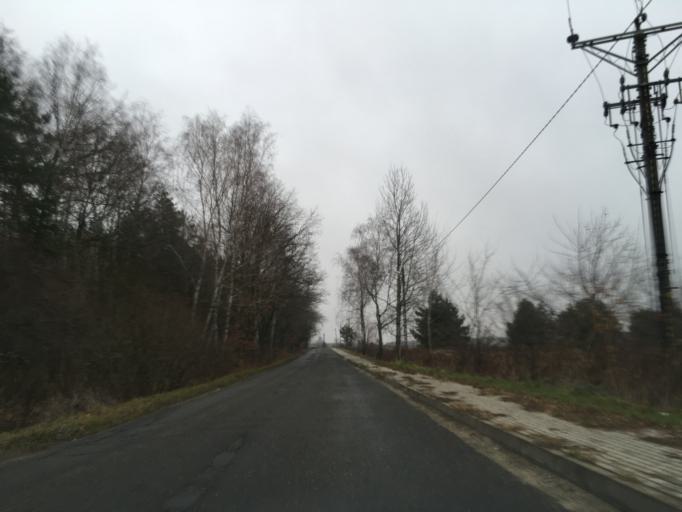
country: PL
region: Masovian Voivodeship
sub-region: Powiat piaseczynski
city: Lesznowola
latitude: 52.0708
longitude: 20.8801
